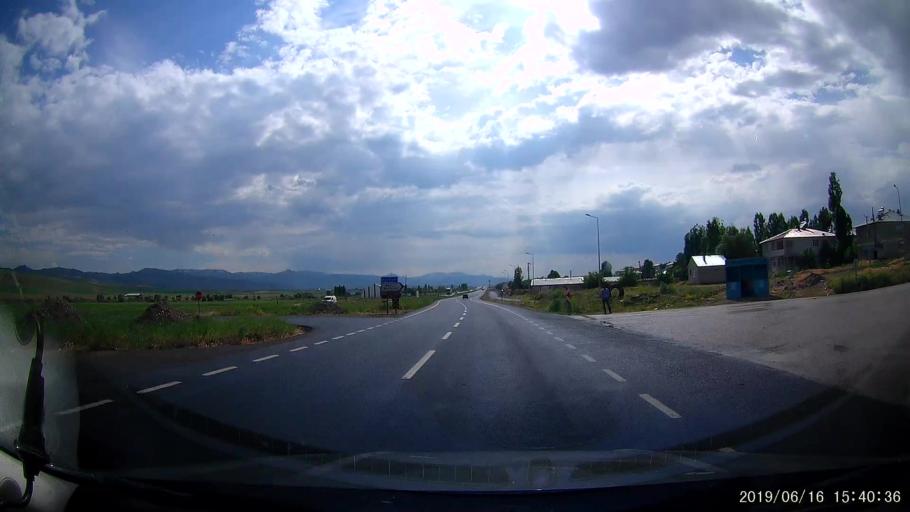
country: TR
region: Erzurum
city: Koprukoy
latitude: 39.9672
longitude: 41.8716
